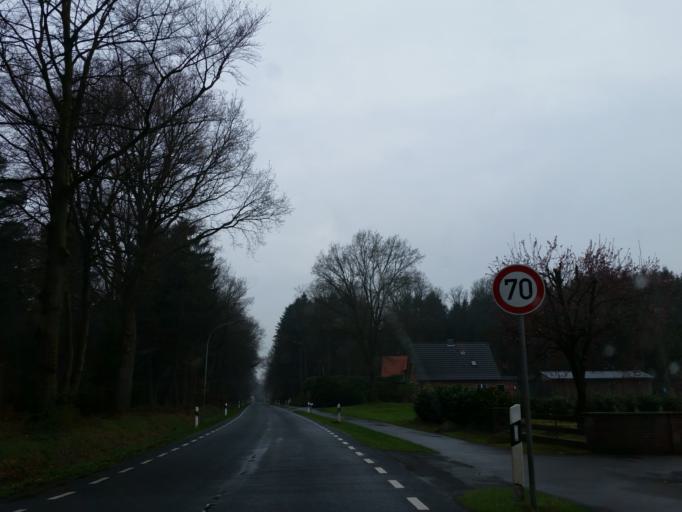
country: DE
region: Lower Saxony
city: Hipstedt
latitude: 53.5220
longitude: 8.9574
